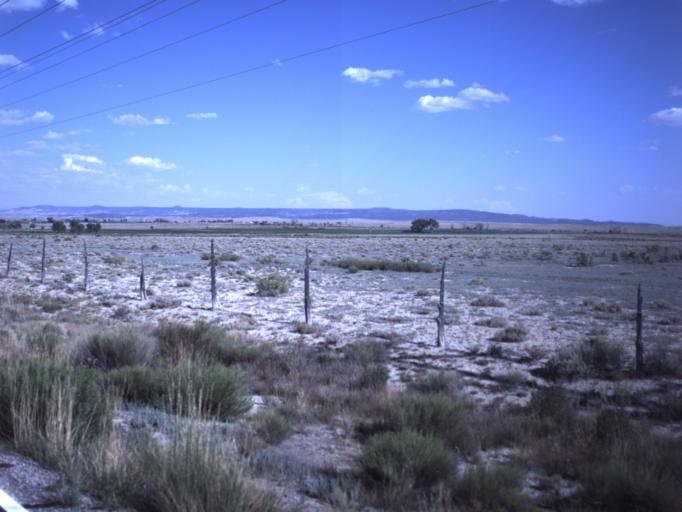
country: US
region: Utah
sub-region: Emery County
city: Huntington
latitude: 39.3450
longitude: -110.9075
